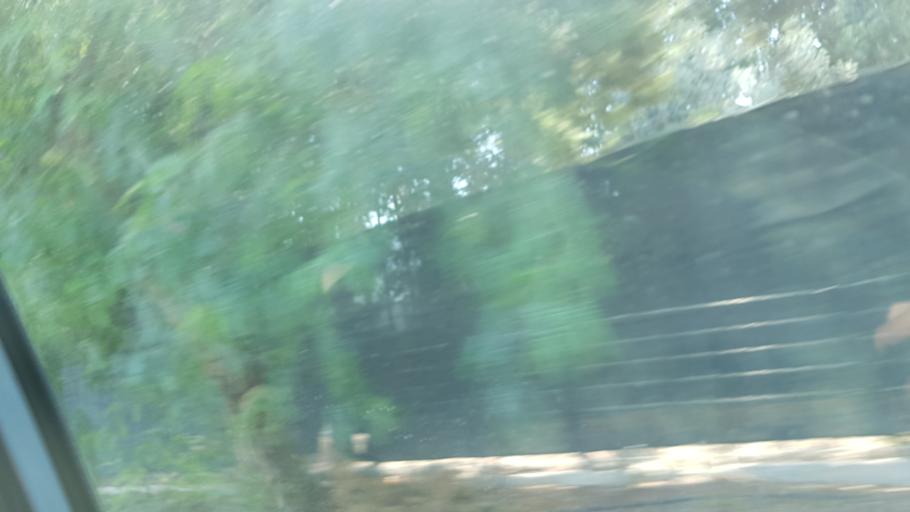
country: TR
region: Izmir
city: Urla
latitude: 38.3808
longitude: 26.7478
